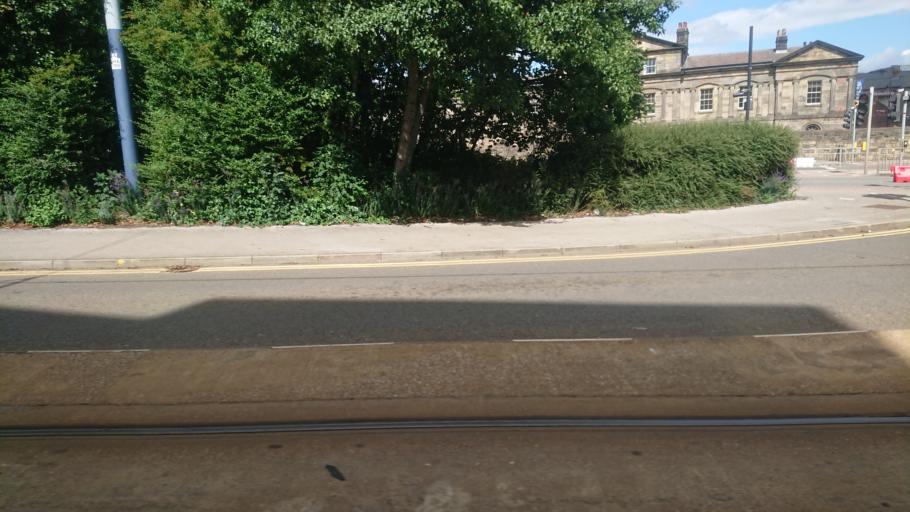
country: GB
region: England
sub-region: Sheffield
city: Sheffield
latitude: 53.3894
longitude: -1.4788
